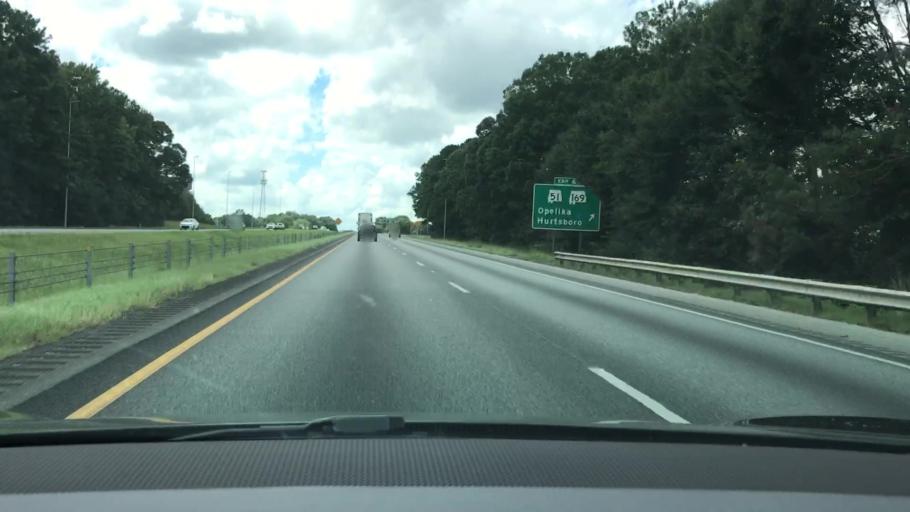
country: US
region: Alabama
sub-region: Lee County
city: Opelika
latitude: 32.6349
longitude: -85.3664
